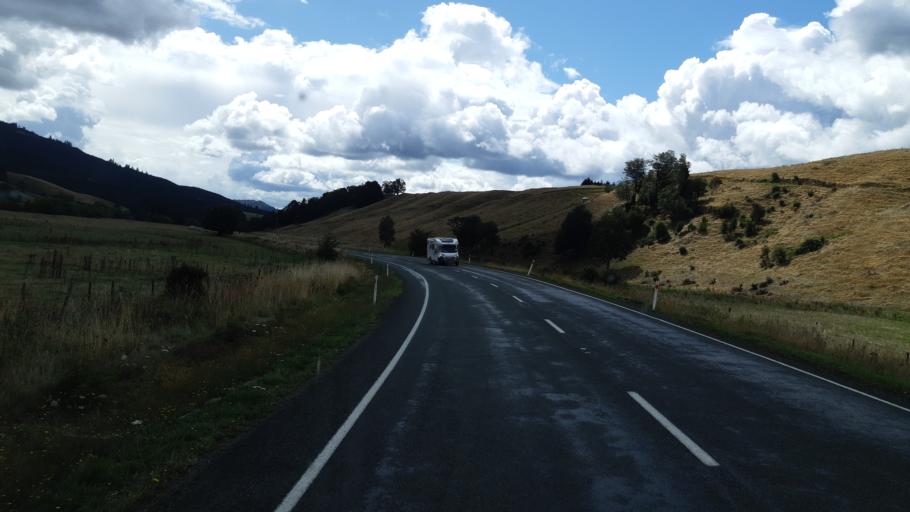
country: NZ
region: Tasman
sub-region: Tasman District
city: Wakefield
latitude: -41.5723
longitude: 172.7745
